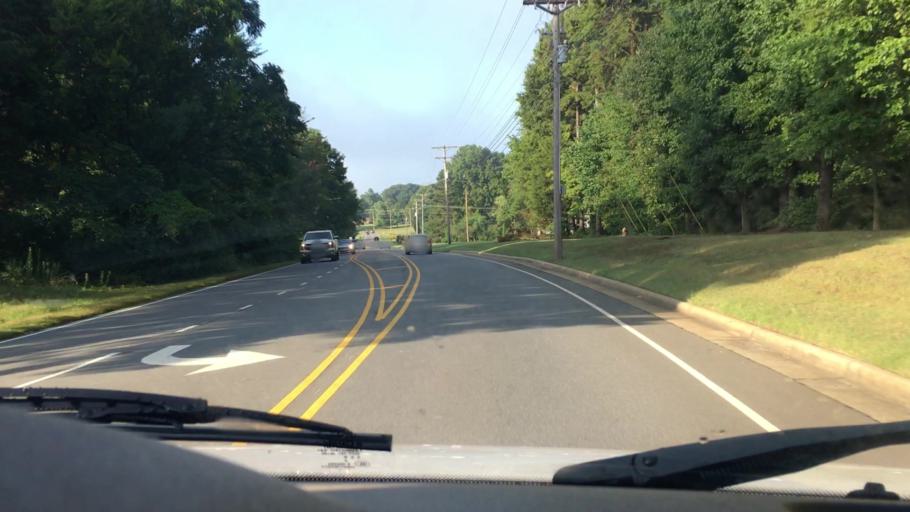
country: US
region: North Carolina
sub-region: Mecklenburg County
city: Huntersville
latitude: 35.4126
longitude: -80.9249
